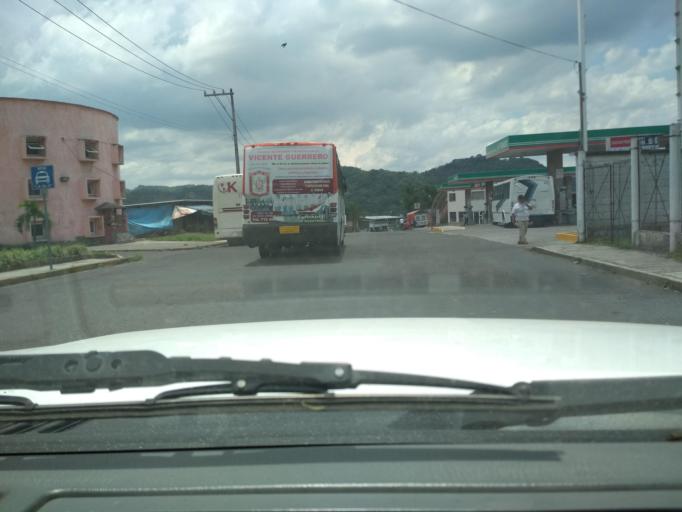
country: MX
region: Veracruz
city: Cordoba
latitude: 18.8847
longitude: -96.9212
